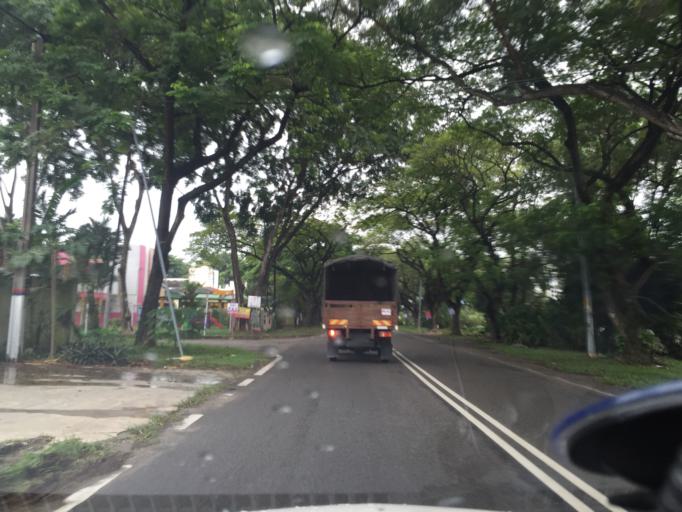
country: MY
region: Selangor
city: Klang
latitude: 3.0097
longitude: 101.4513
